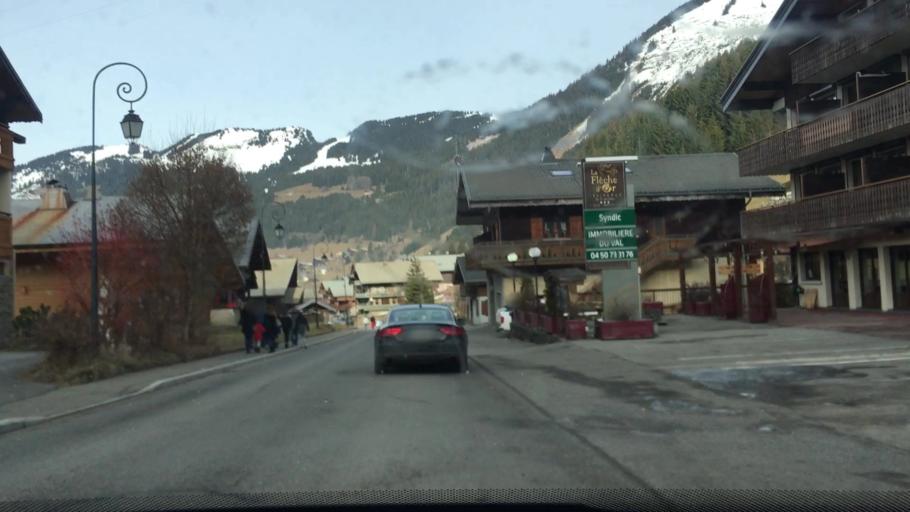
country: FR
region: Rhone-Alpes
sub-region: Departement de la Haute-Savoie
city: Chatel
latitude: 46.2584
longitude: 6.8406
